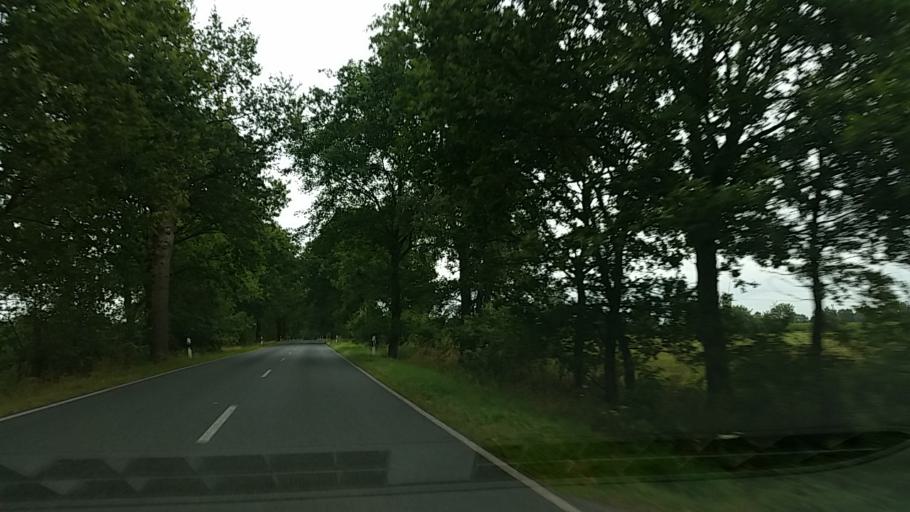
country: DE
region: Lower Saxony
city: Vollersode
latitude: 53.4039
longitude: 8.9202
